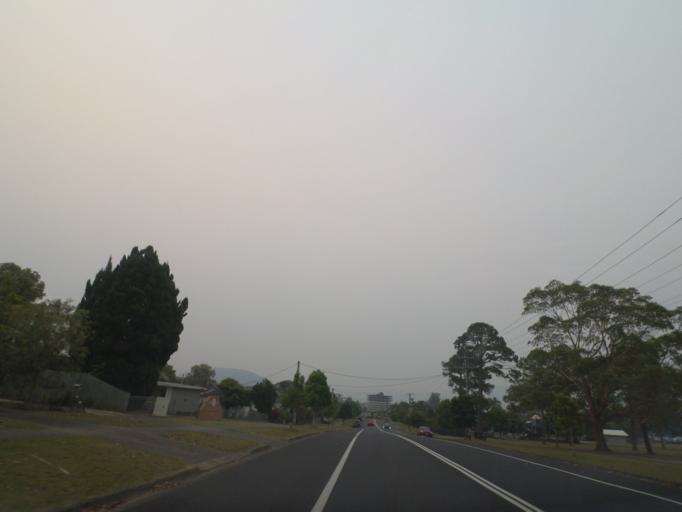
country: AU
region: New South Wales
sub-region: Coffs Harbour
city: Coffs Harbour
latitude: -30.3022
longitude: 153.1180
